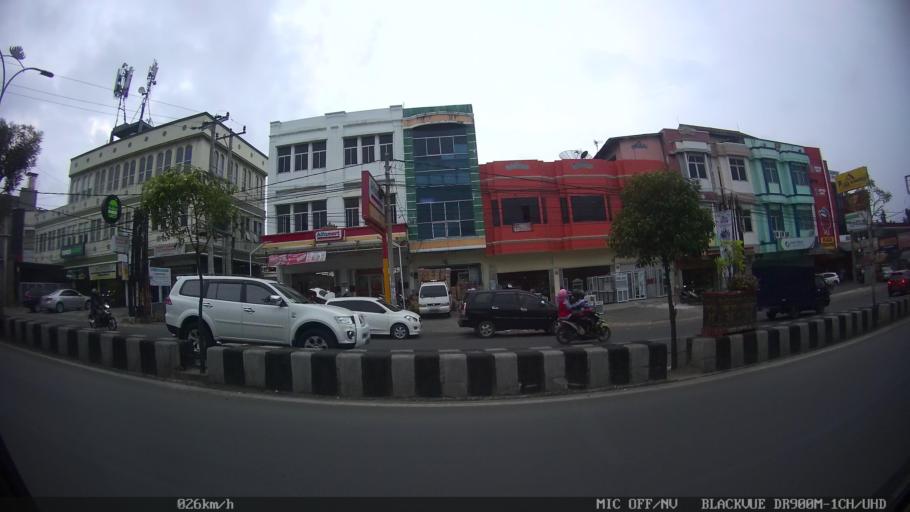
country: ID
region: Lampung
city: Bandarlampung
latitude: -5.4071
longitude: 105.2743
